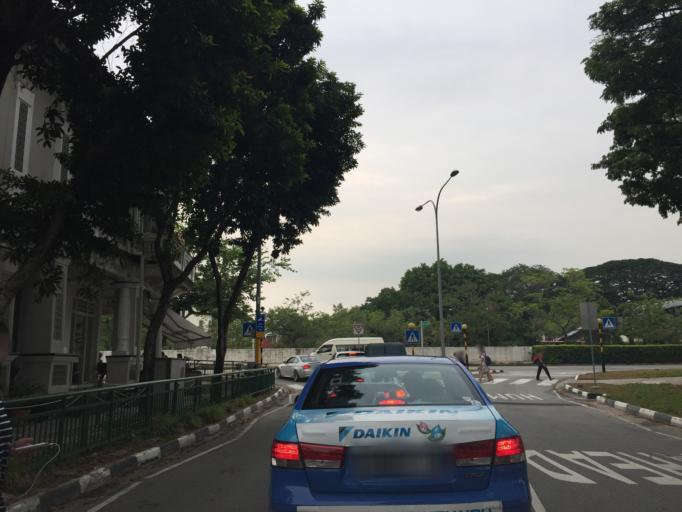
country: SG
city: Singapore
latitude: 1.3225
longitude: 103.8146
